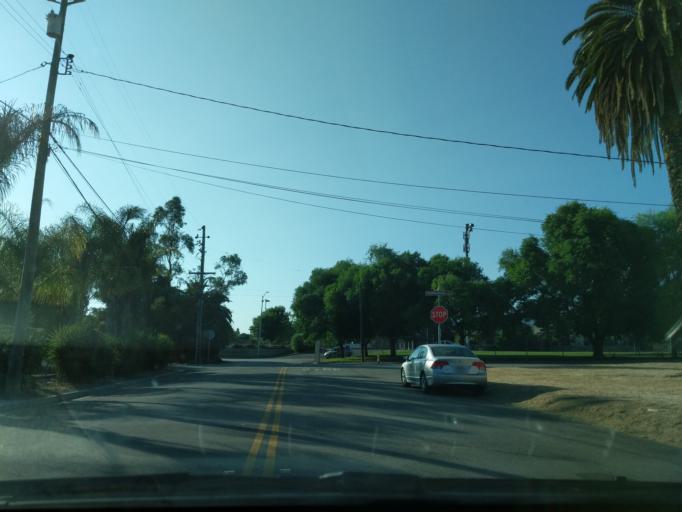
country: US
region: California
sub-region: San Luis Obispo County
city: San Luis Obispo
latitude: 35.2888
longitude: -120.6633
